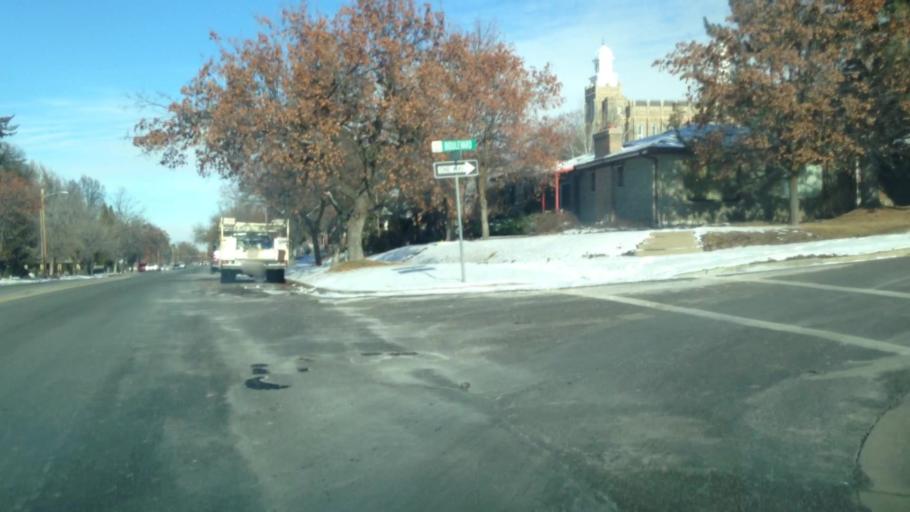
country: US
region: Utah
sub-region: Cache County
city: Logan
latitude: 41.7316
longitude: -111.8297
